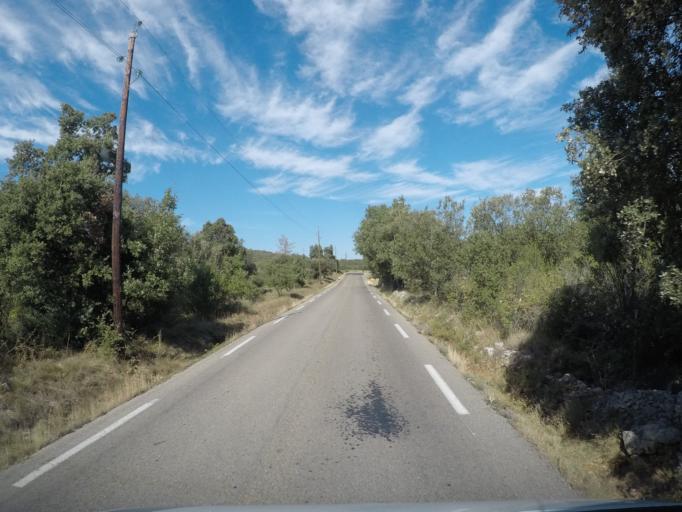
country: FR
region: Languedoc-Roussillon
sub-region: Departement du Gard
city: Anduze
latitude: 44.0074
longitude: 3.9836
